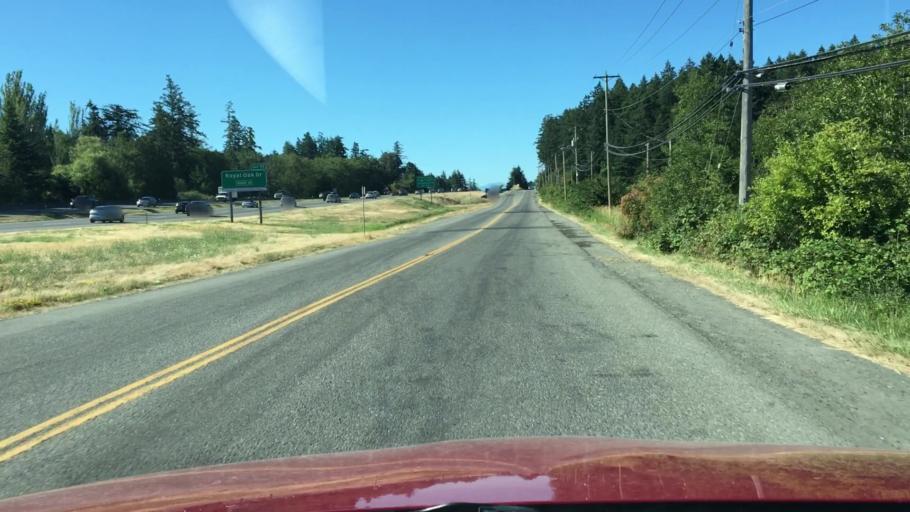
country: CA
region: British Columbia
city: Victoria
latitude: 48.5121
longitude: -123.3844
